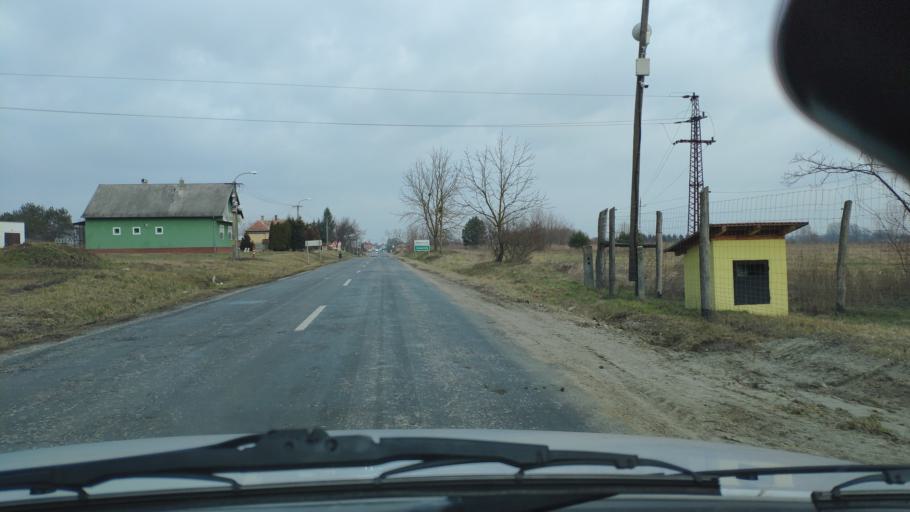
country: HU
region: Zala
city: Nagykanizsa
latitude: 46.4486
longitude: 16.9391
